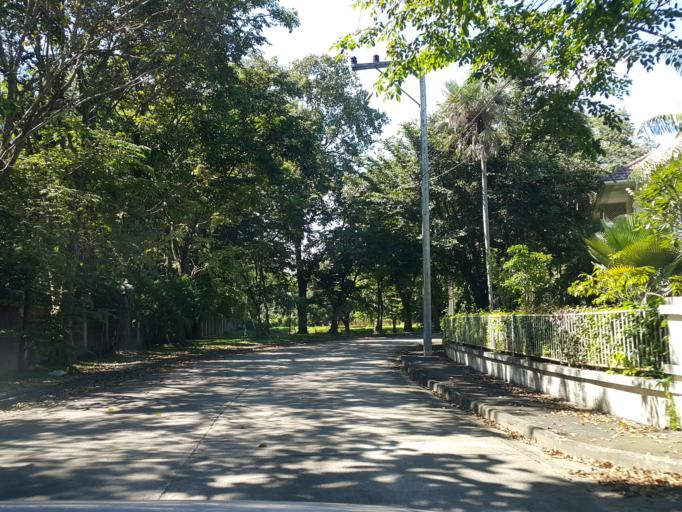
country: TH
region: Chiang Mai
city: San Sai
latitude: 18.8491
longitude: 99.0040
